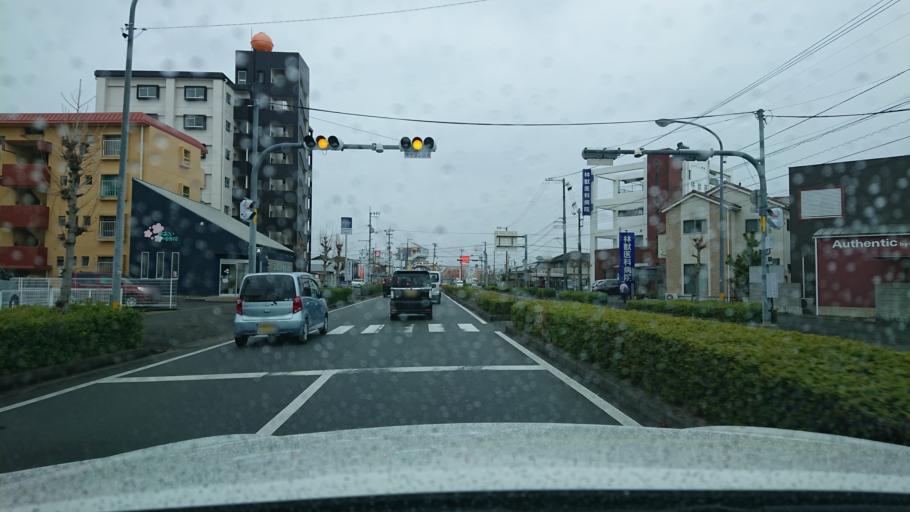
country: JP
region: Tokushima
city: Tokushima-shi
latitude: 34.0815
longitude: 134.5113
